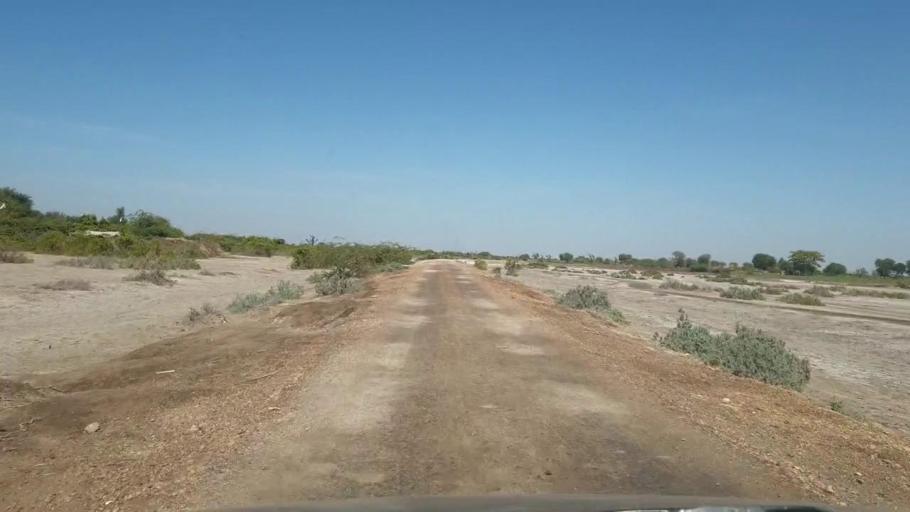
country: PK
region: Sindh
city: Dhoro Naro
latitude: 25.4089
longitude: 69.6166
